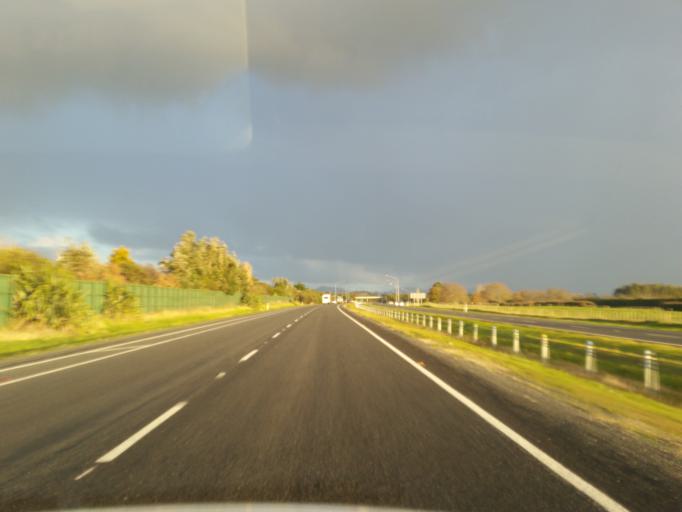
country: NZ
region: Waikato
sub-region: Waikato District
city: Te Kauwhata
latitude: -37.4815
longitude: 175.1603
